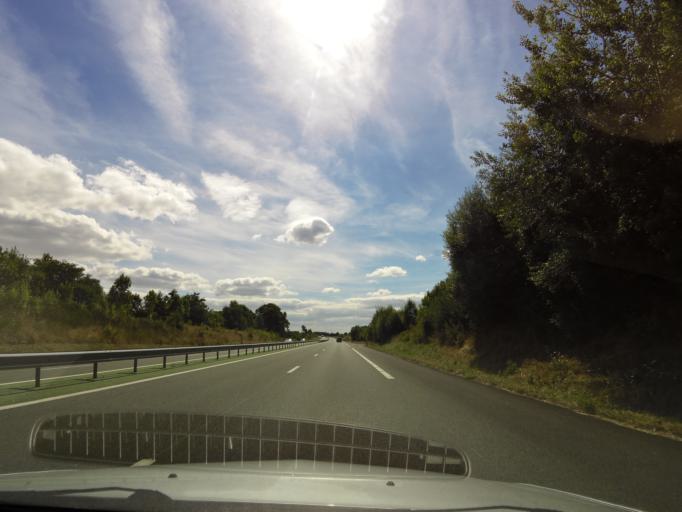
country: FR
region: Pays de la Loire
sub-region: Departement de la Vendee
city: Les Essarts
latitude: 46.7798
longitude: -1.2579
